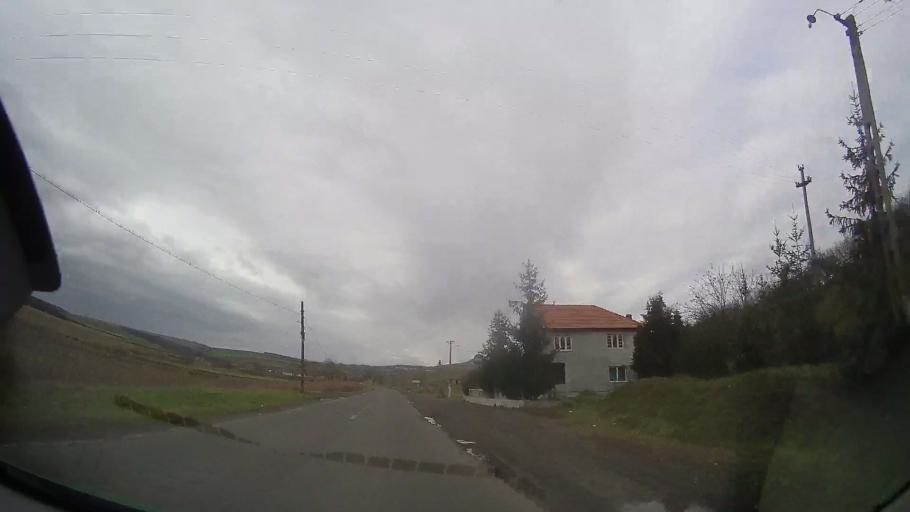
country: RO
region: Bistrita-Nasaud
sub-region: Comuna Urmenis
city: Urmenis
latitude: 46.7676
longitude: 24.3665
